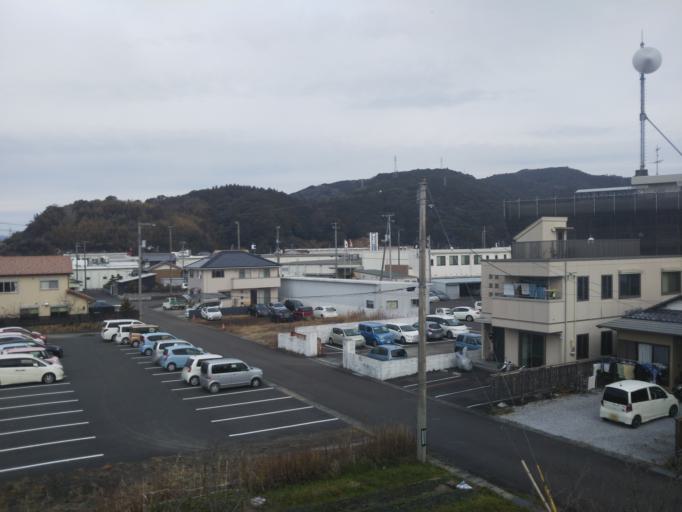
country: JP
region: Kochi
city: Nakamura
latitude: 32.9812
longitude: 132.9544
